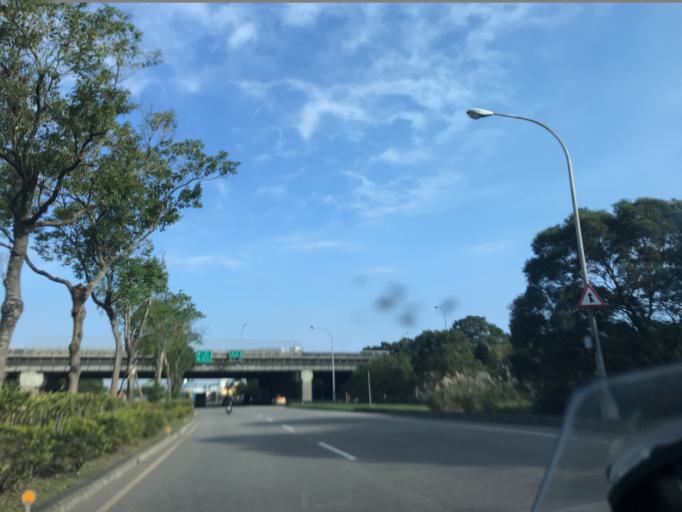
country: TW
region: Taiwan
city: Daxi
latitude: 24.8603
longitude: 121.2232
